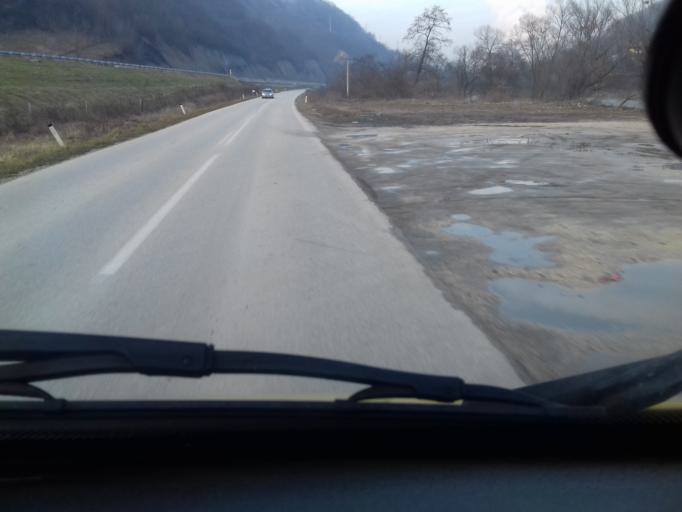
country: BA
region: Federation of Bosnia and Herzegovina
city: Dobrinje
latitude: 44.0578
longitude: 18.1037
